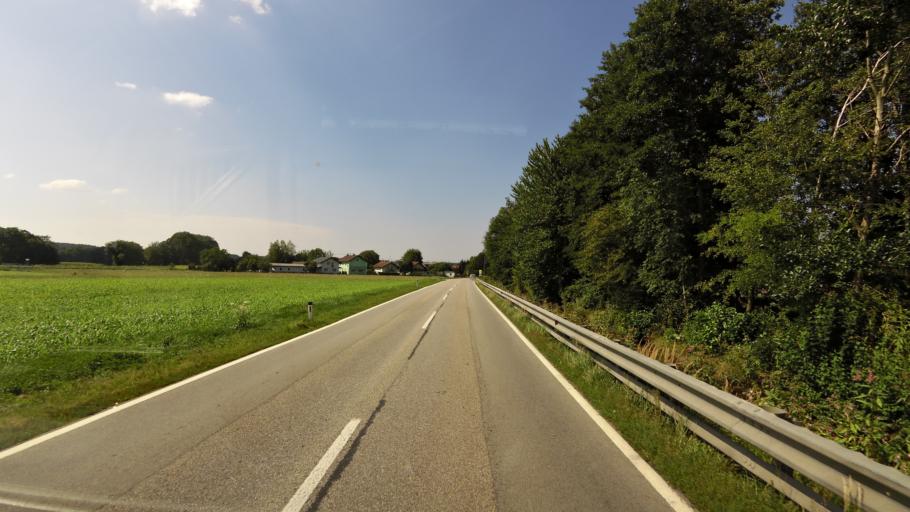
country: AT
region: Upper Austria
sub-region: Politischer Bezirk Braunau am Inn
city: Altheim
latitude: 48.1368
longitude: 13.1393
